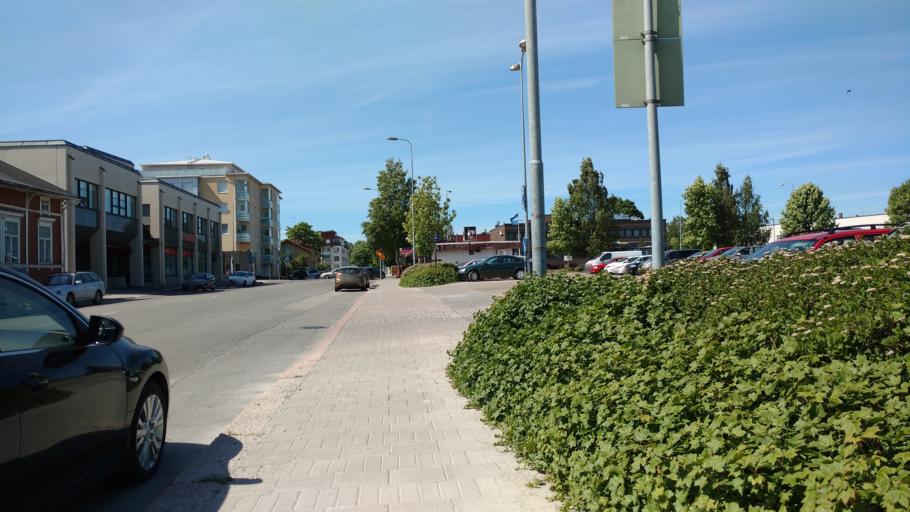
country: FI
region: Varsinais-Suomi
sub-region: Salo
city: Salo
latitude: 60.3882
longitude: 23.1276
